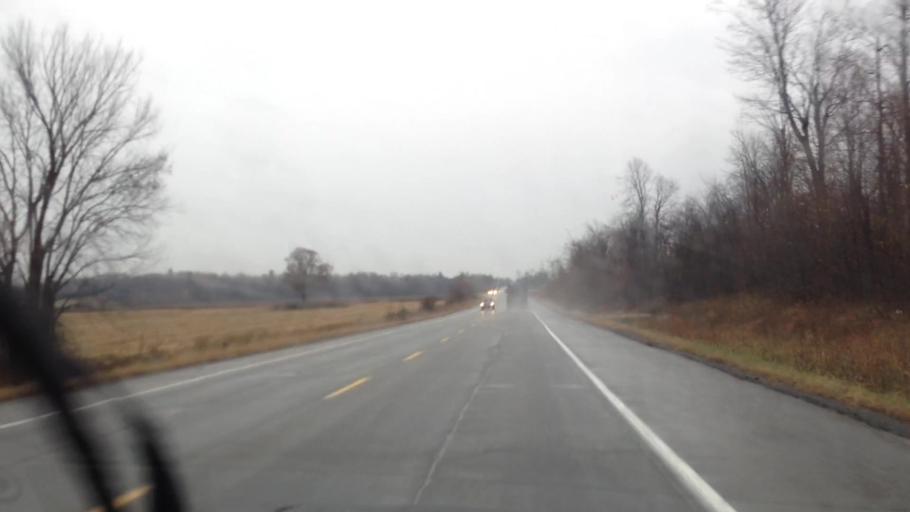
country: CA
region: Ontario
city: Clarence-Rockland
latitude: 45.3900
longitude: -75.3903
